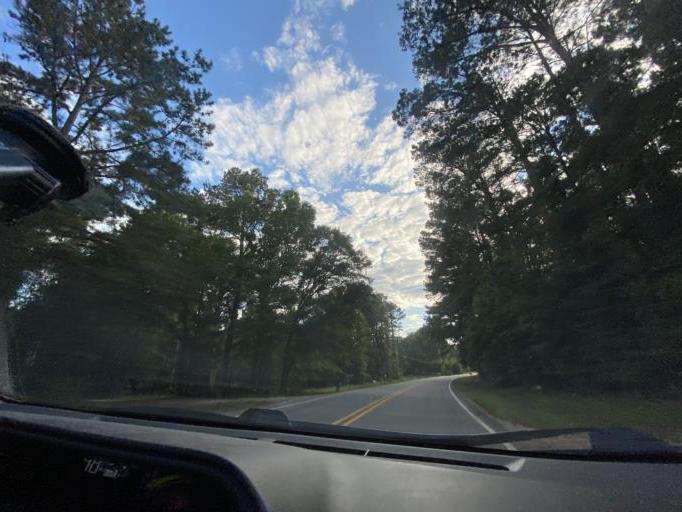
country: US
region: Georgia
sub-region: Fayette County
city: Peachtree City
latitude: 33.4112
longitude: -84.6548
